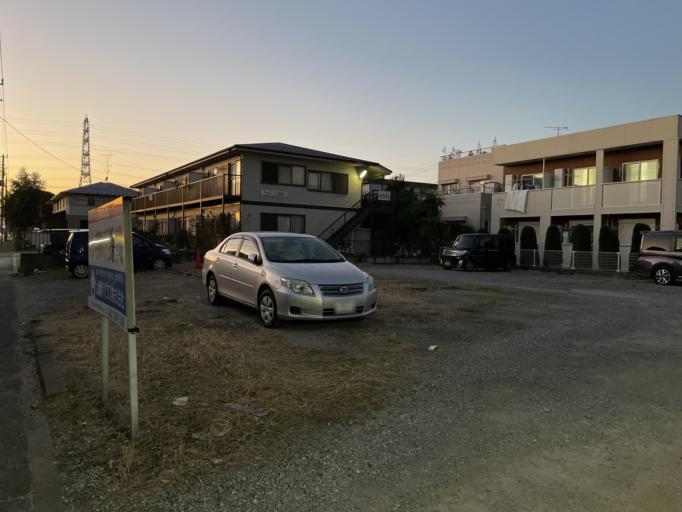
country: JP
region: Chiba
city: Nagareyama
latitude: 35.8235
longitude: 139.9106
